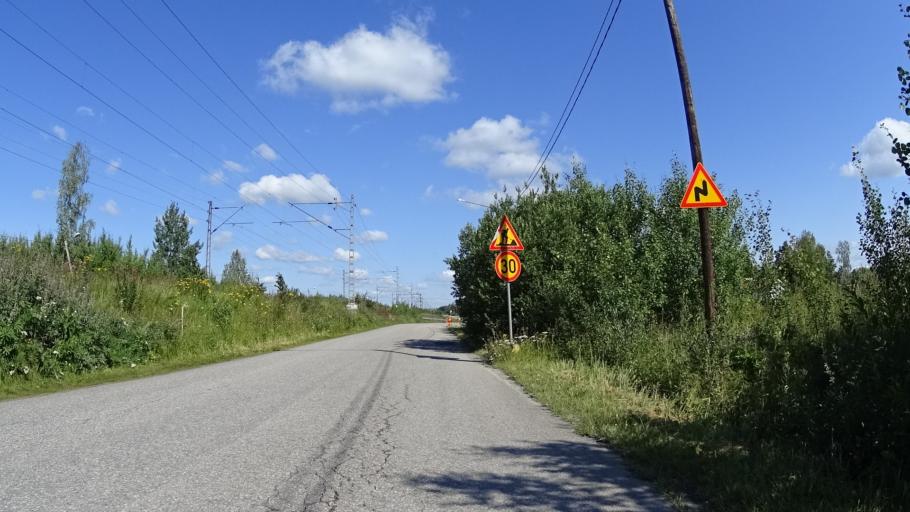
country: FI
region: Uusimaa
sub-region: Helsinki
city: Jaervenpaeae
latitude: 60.4491
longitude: 25.1040
